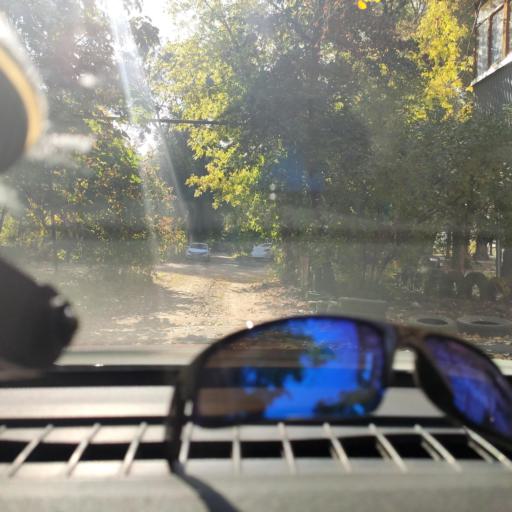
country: RU
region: Samara
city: Petra-Dubrava
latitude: 53.2351
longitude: 50.2877
